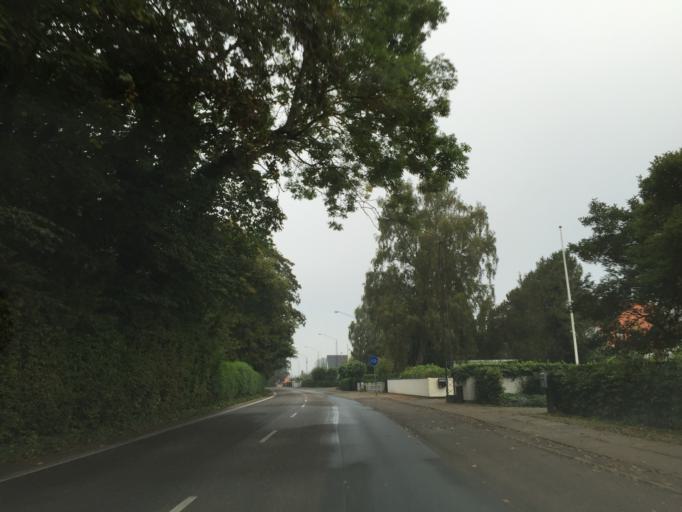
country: DK
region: South Denmark
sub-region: Sonderborg Kommune
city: Sonderborg
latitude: 54.9021
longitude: 9.7969
